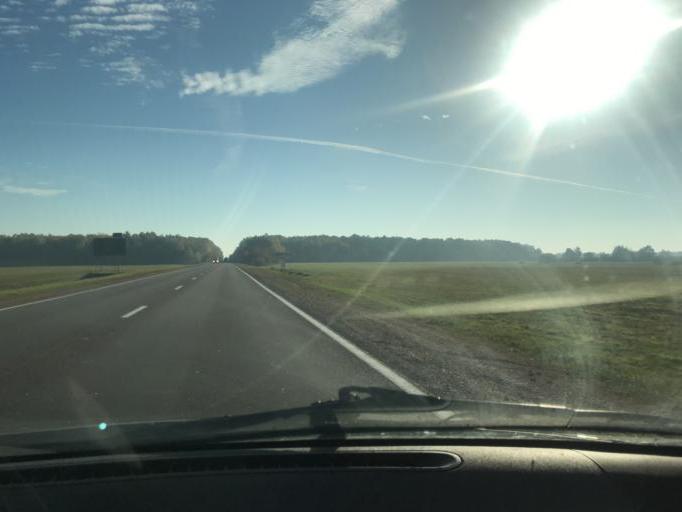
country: BY
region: Brest
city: Ivanava
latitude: 52.1542
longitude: 25.3473
